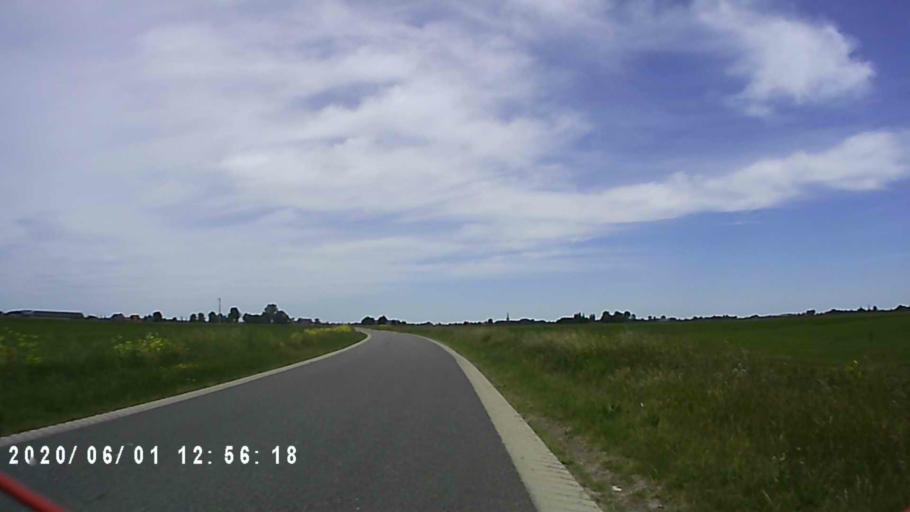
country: NL
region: Friesland
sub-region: Gemeente Franekeradeel
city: Tzum
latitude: 53.1447
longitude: 5.5299
